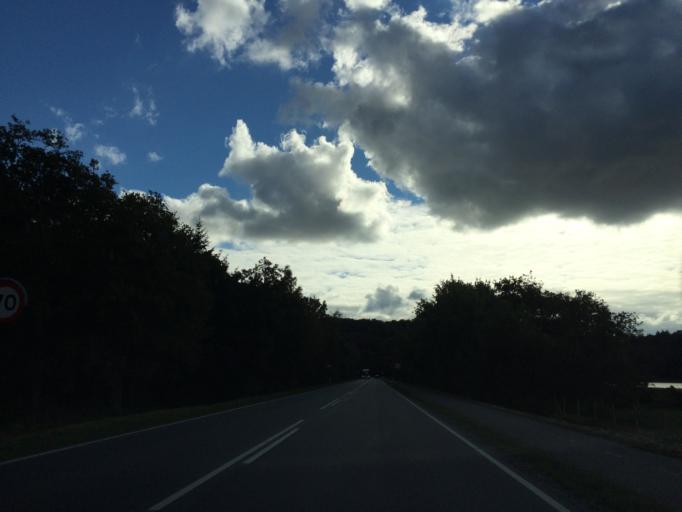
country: DK
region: Central Jutland
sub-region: Skanderborg Kommune
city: Ry
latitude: 56.1027
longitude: 9.7847
